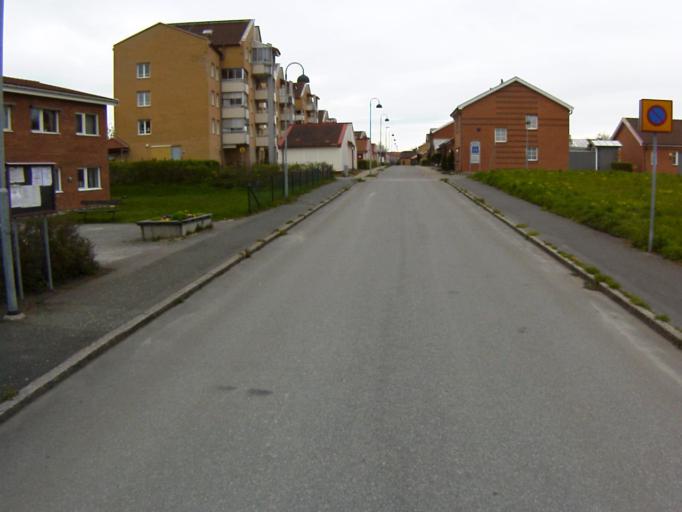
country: SE
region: Skane
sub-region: Kristianstads Kommun
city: Kristianstad
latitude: 56.0200
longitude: 14.1385
